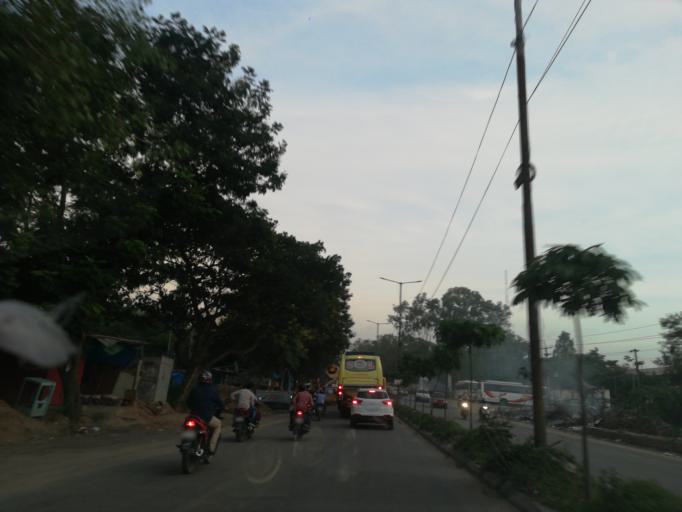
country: IN
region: Telangana
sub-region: Rangareddi
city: Kukatpalli
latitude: 17.5135
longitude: 78.3609
